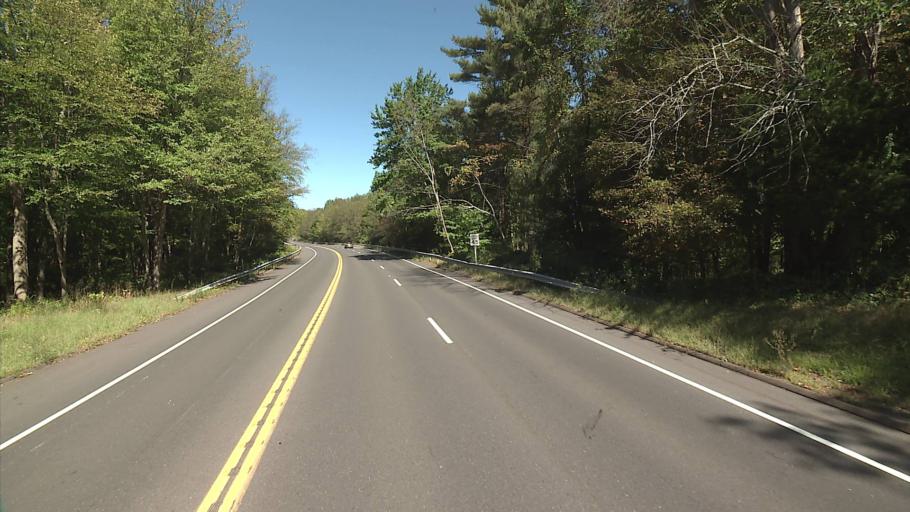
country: US
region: Connecticut
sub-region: New Haven County
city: Woodbridge
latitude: 41.3908
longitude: -72.9718
